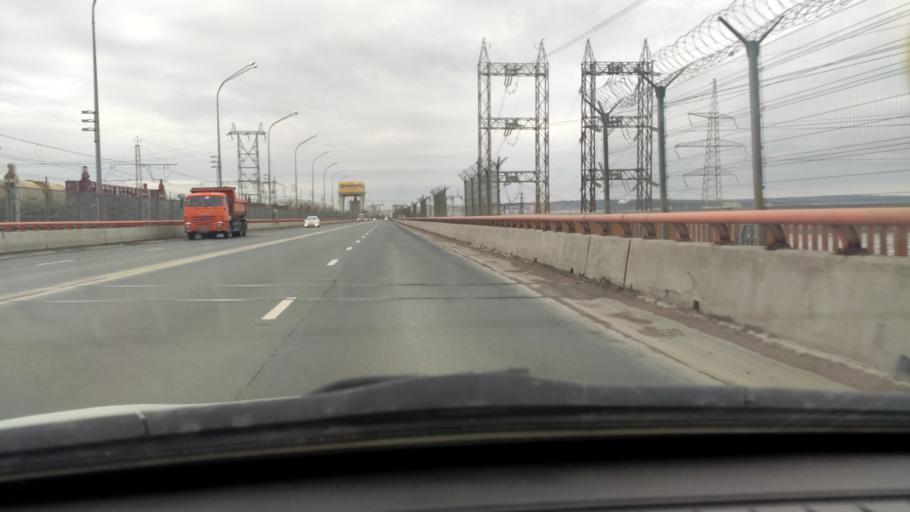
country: RU
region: Samara
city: Zhigulevsk
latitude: 53.4557
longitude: 49.4969
